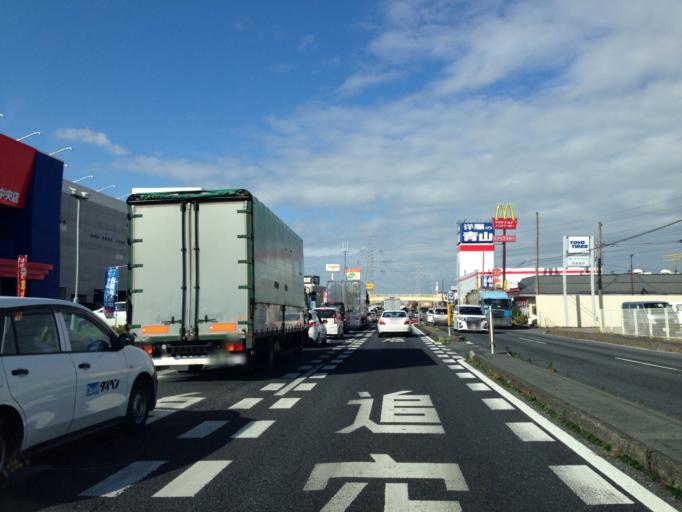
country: JP
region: Chiba
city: Kashiwa
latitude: 35.8816
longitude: 139.9656
